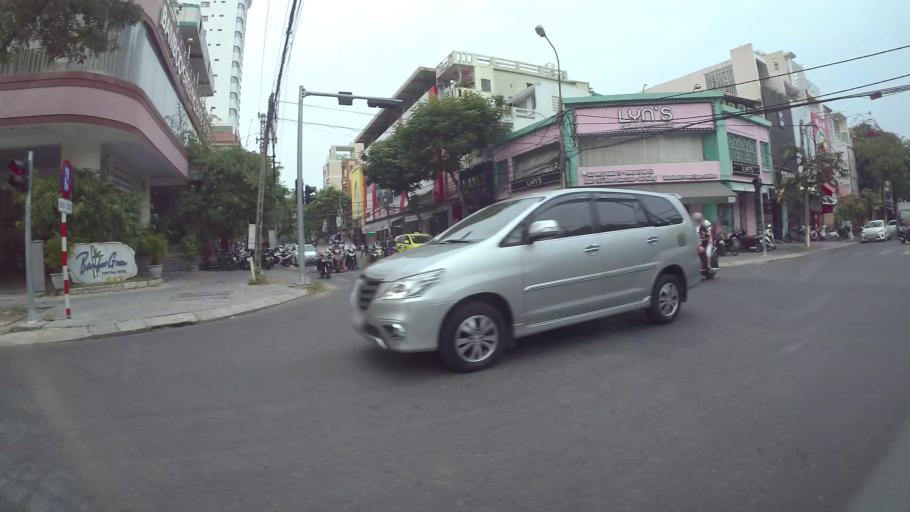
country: VN
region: Da Nang
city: Da Nang
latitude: 16.0630
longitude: 108.2197
